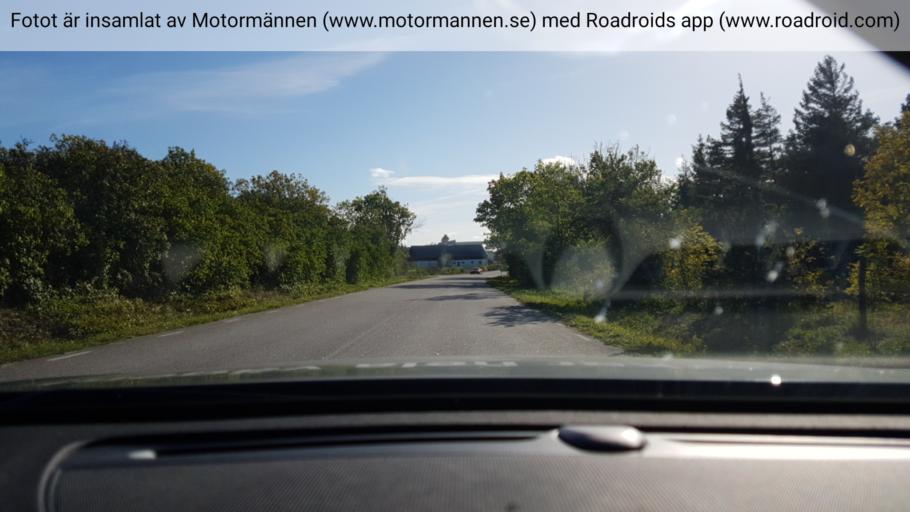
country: SE
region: Gotland
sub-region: Gotland
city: Slite
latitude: 57.8472
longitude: 18.8069
